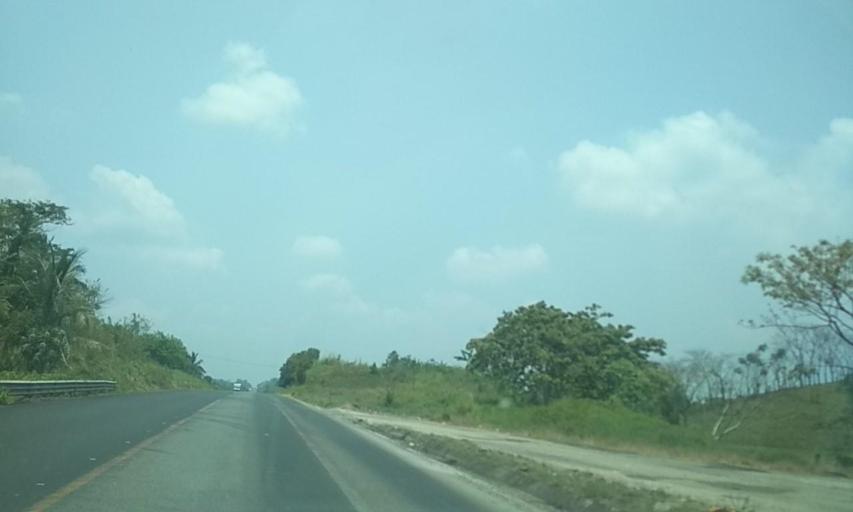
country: MX
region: Tabasco
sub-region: Huimanguillo
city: Francisco Rueda
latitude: 17.7162
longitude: -93.9479
